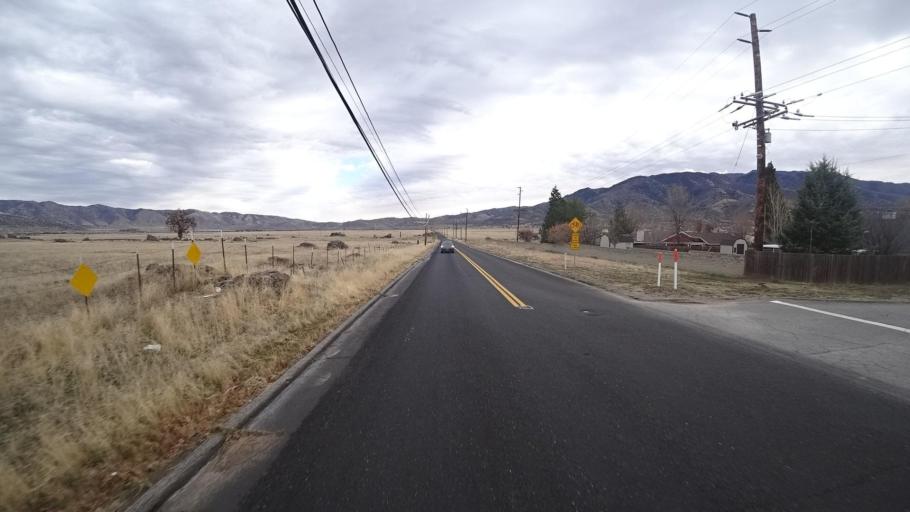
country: US
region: California
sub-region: Kern County
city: Stallion Springs
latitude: 35.0946
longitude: -118.6390
